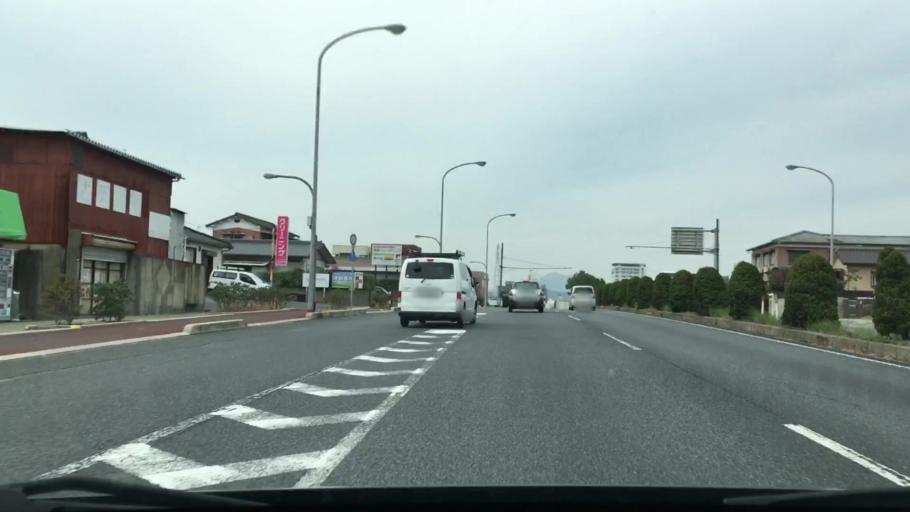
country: JP
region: Yamaguchi
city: Tokuyama
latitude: 34.0410
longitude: 131.8413
